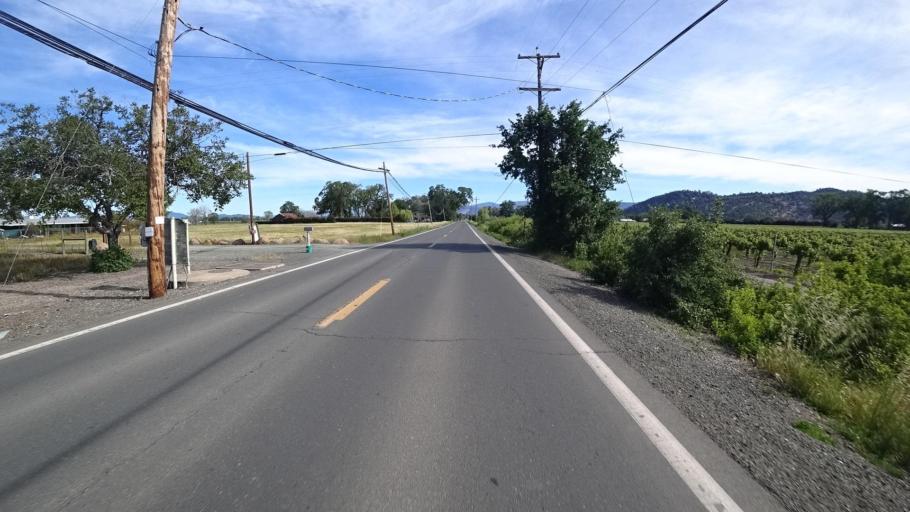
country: US
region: California
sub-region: Lake County
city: Kelseyville
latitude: 38.9854
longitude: -122.8291
